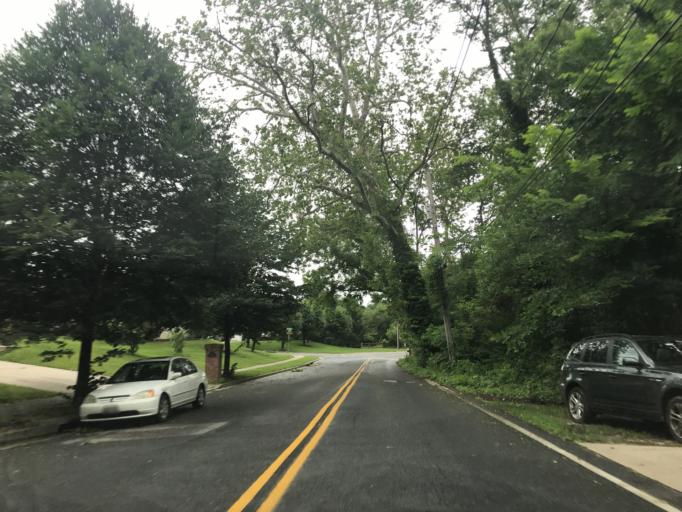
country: US
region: Maryland
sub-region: Anne Arundel County
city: Linthicum
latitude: 39.2093
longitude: -76.6544
